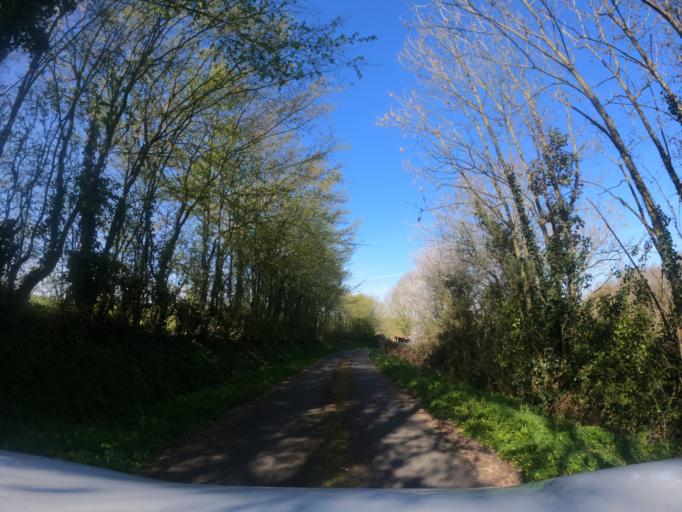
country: FR
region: Pays de la Loire
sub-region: Departement de la Vendee
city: Montournais
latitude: 46.7132
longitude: -0.7597
